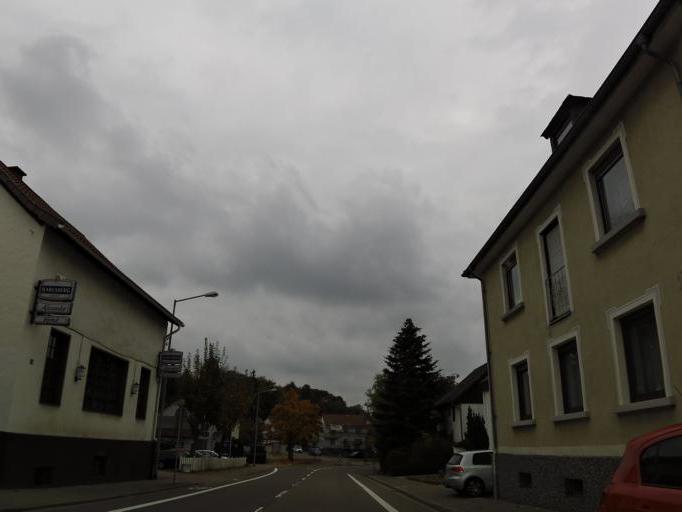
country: DE
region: Saarland
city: Sankt Ingbert
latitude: 49.2647
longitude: 7.1025
